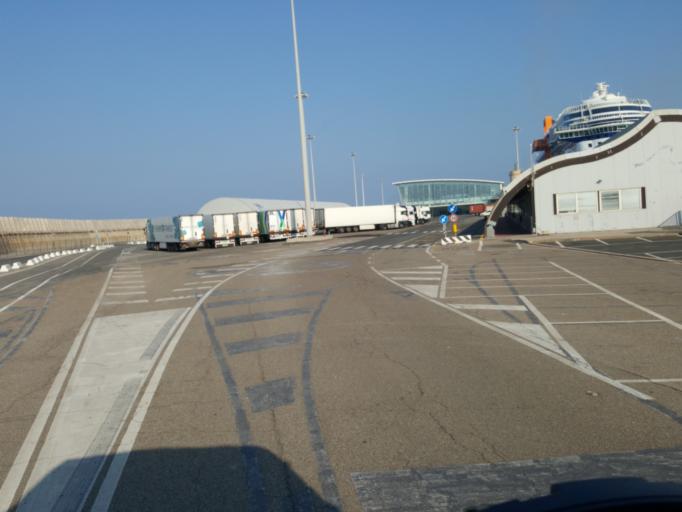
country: IT
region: Latium
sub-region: Citta metropolitana di Roma Capitale
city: Civitavecchia
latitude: 42.0930
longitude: 11.7813
